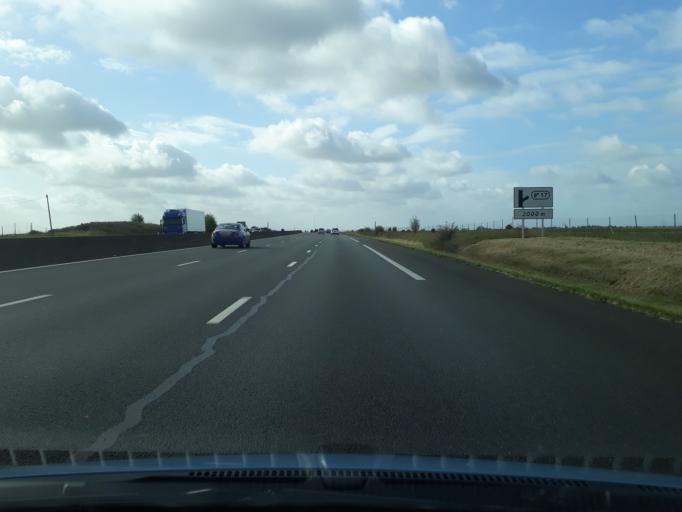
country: FR
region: Centre
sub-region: Departement du Loir-et-Cher
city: La Chaussee-Saint-Victor
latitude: 47.6423
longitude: 1.3629
